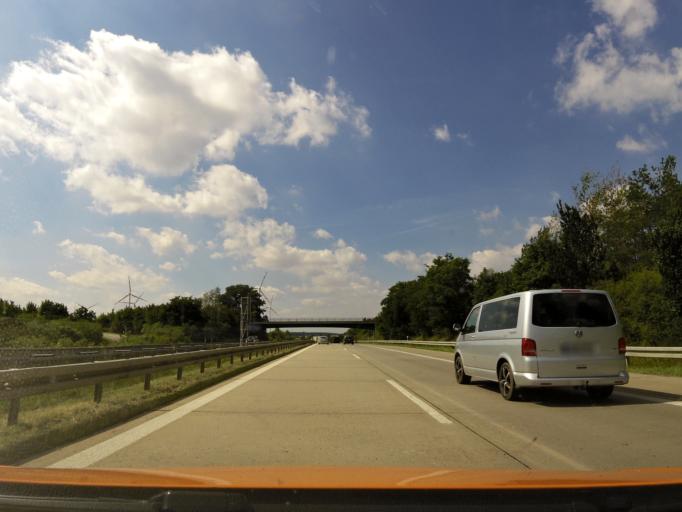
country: PL
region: West Pomeranian Voivodeship
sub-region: Powiat policki
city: Kolbaskowo
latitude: 53.3331
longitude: 14.3894
